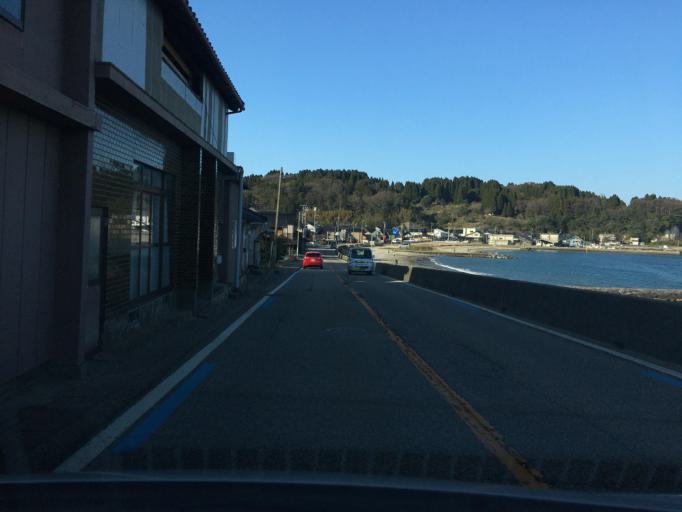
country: JP
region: Toyama
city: Himi
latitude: 36.9095
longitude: 137.0170
